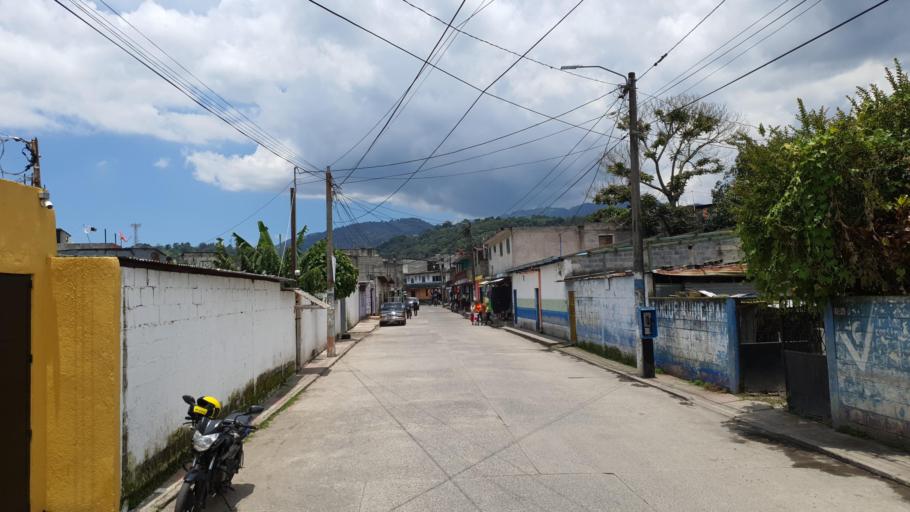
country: GT
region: Guatemala
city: Villa Canales
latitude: 14.4783
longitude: -90.5366
